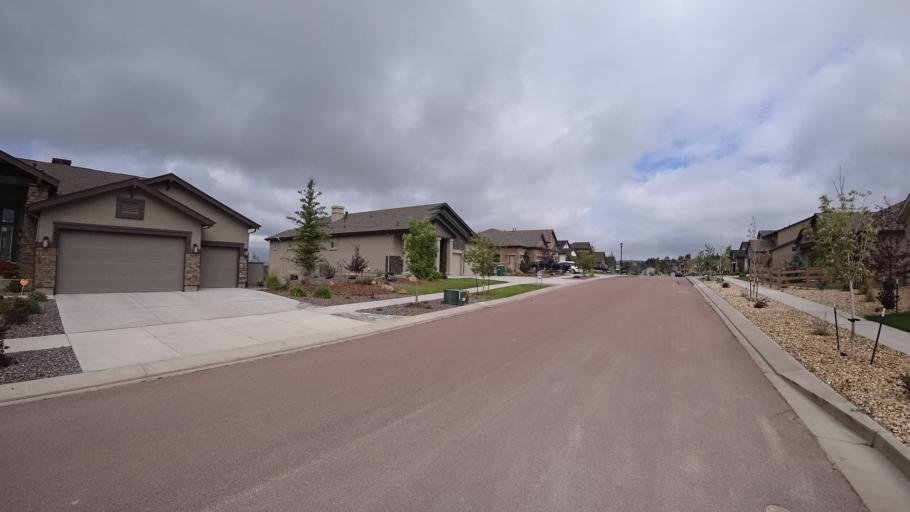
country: US
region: Colorado
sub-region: El Paso County
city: Gleneagle
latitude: 39.0116
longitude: -104.7928
